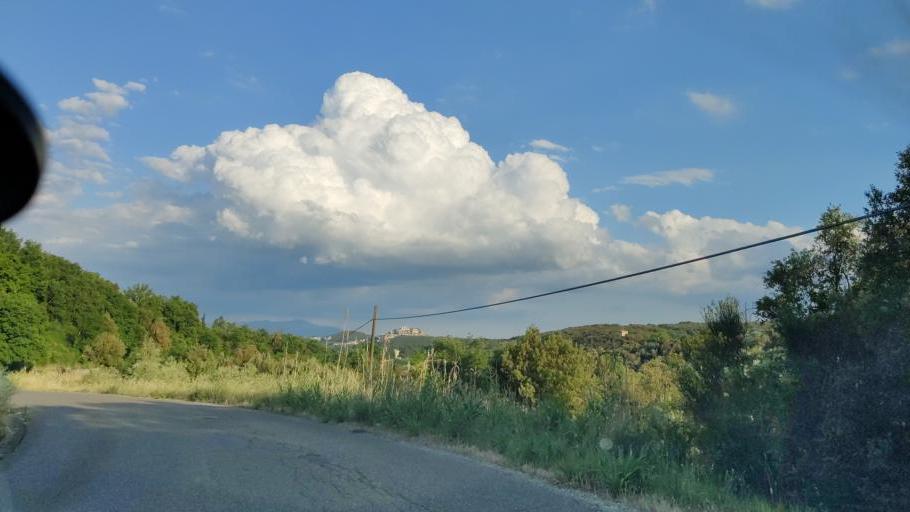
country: IT
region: Umbria
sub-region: Provincia di Terni
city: Amelia
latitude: 42.5804
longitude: 12.3903
